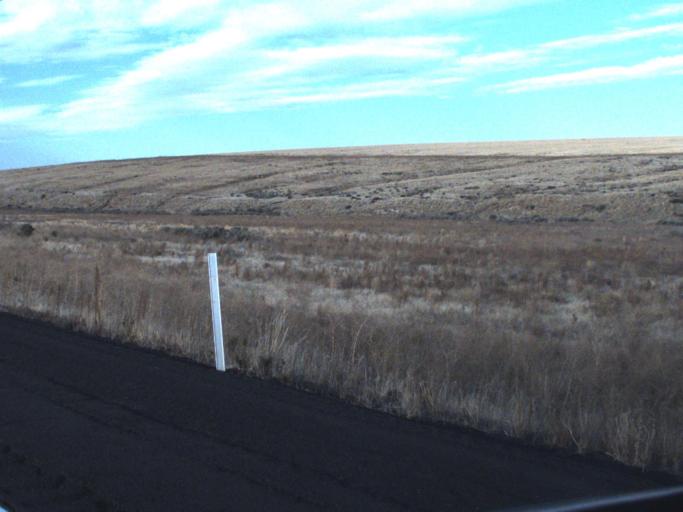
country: US
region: Washington
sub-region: Franklin County
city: Connell
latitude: 46.8270
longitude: -118.6670
